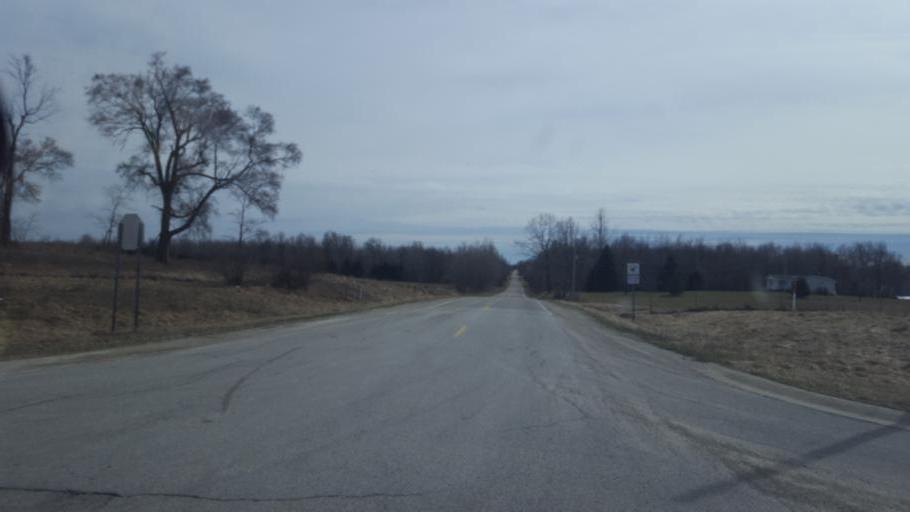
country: US
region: Michigan
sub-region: Isabella County
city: Lake Isabella
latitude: 43.5958
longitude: -85.0267
